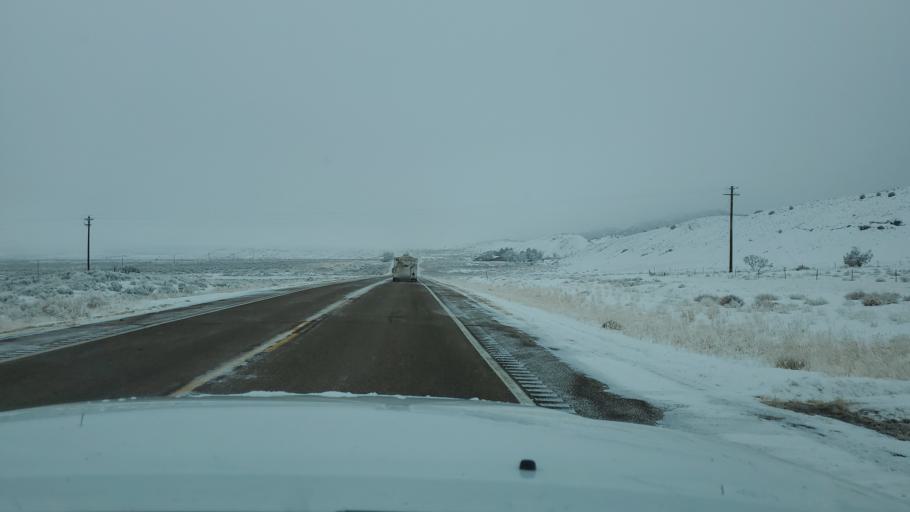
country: US
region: Colorado
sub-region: Rio Blanco County
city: Rangely
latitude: 40.2427
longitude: -108.9649
